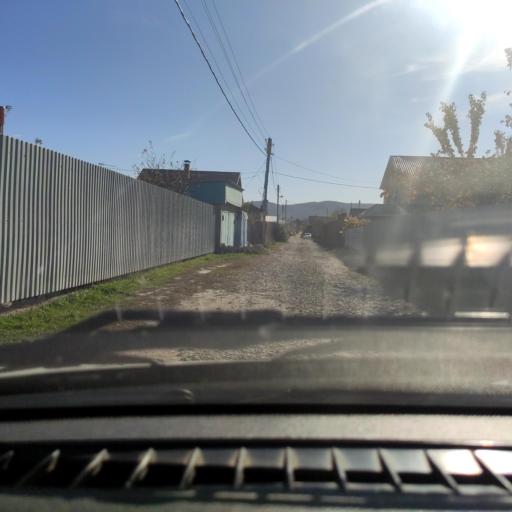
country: RU
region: Samara
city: Zhigulevsk
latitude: 53.4678
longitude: 49.5869
